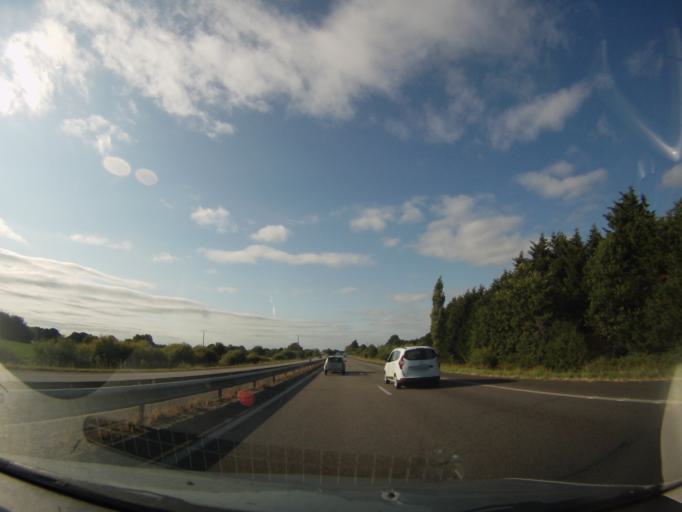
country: FR
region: Pays de la Loire
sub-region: Departement de la Loire-Atlantique
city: Heric
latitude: 47.4408
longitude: -1.6401
